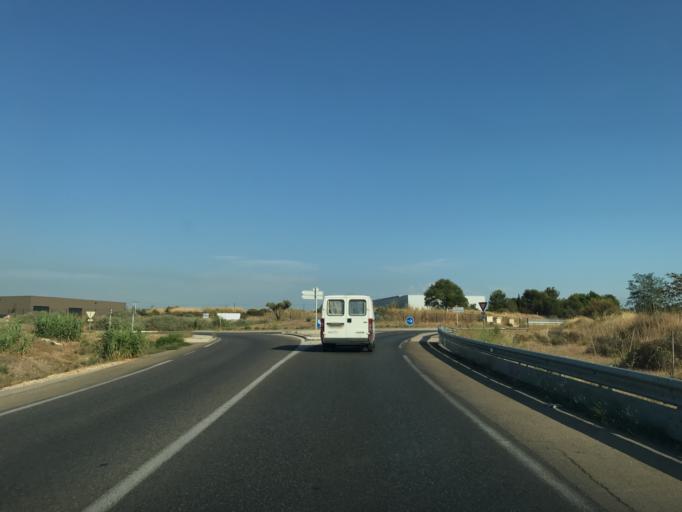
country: FR
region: Provence-Alpes-Cote d'Azur
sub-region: Departement des Bouches-du-Rhone
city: Saint-Chamas
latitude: 43.5380
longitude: 5.0461
